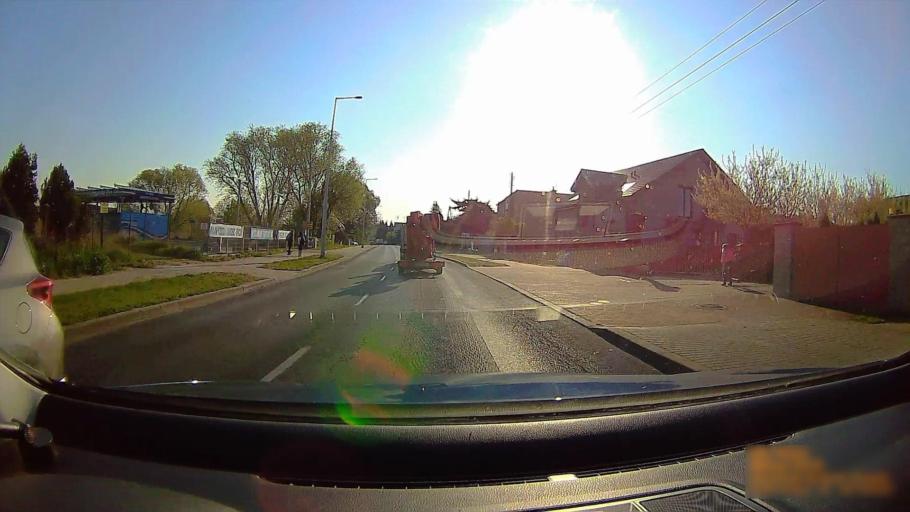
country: PL
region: Greater Poland Voivodeship
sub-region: Konin
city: Konin
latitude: 52.2027
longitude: 18.2388
